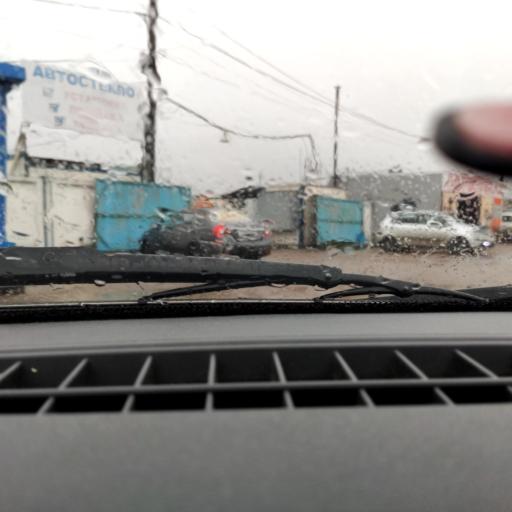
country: RU
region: Bashkortostan
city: Ufa
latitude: 54.8315
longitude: 56.0945
